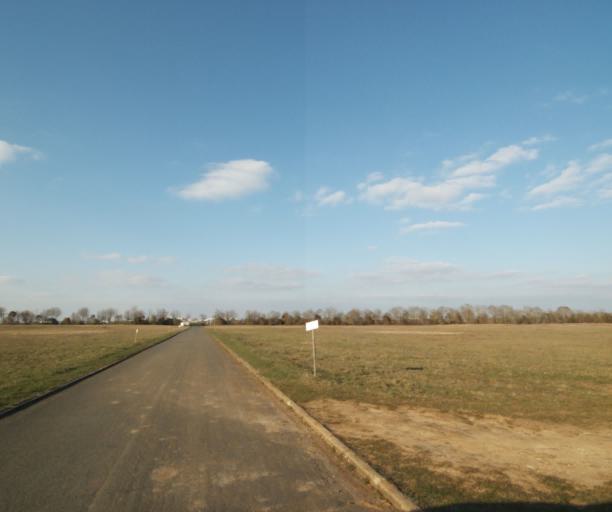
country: FR
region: Poitou-Charentes
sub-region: Departement des Deux-Sevres
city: Aiffres
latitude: 46.3161
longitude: -0.3993
